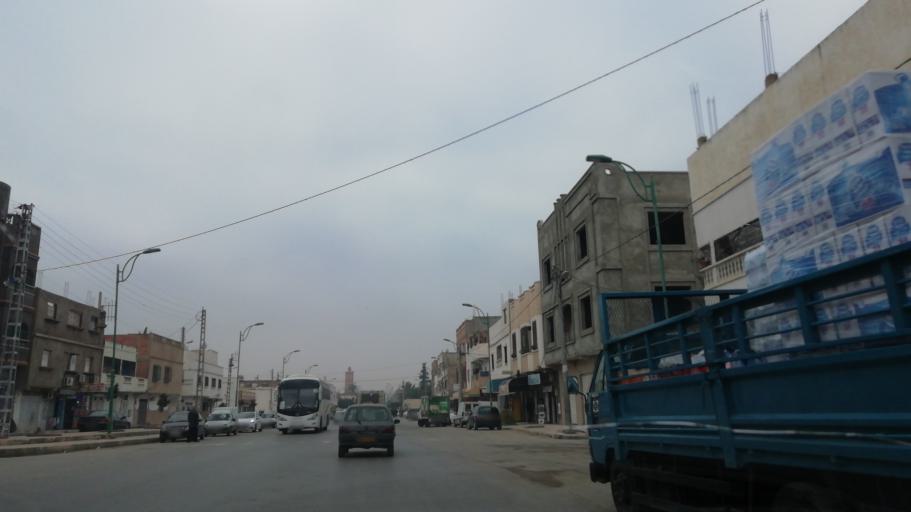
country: DZ
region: Relizane
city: Djidiouia
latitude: 35.9087
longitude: 0.7784
